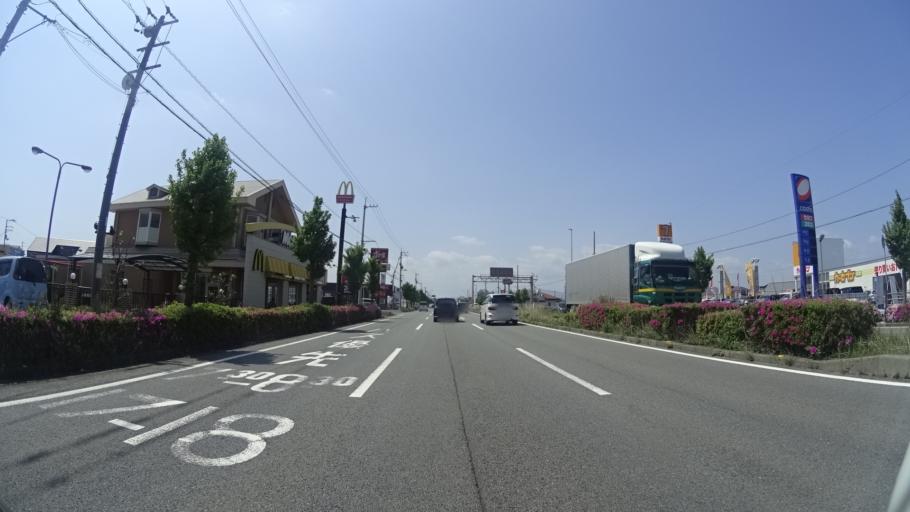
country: JP
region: Tokushima
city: Tokushima-shi
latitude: 34.1111
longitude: 134.5771
